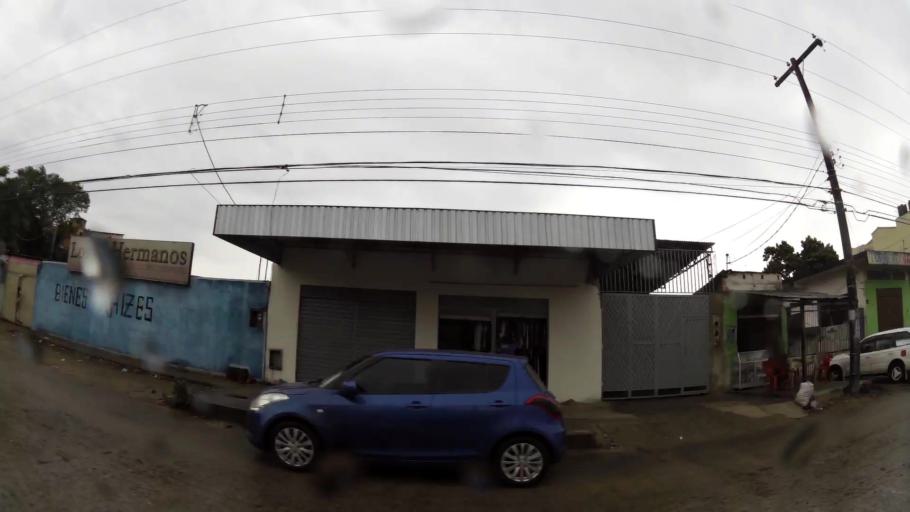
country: BO
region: Santa Cruz
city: Santa Cruz de la Sierra
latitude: -17.8159
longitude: -63.1902
